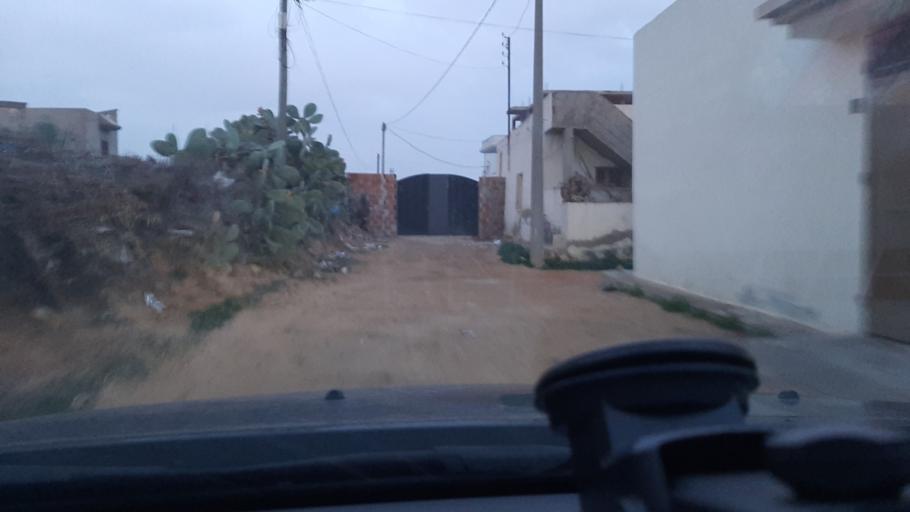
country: TN
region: Safaqis
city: Sfax
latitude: 34.7710
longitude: 10.6811
